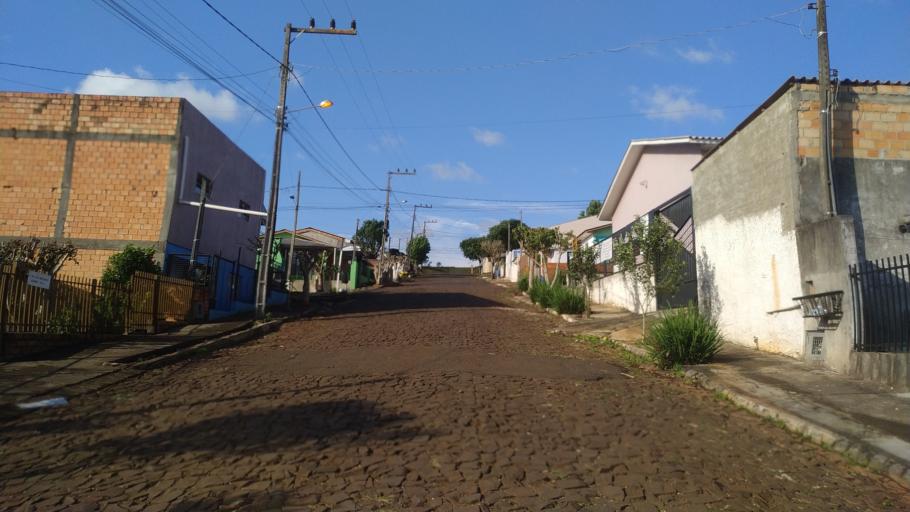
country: BR
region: Santa Catarina
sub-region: Chapeco
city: Chapeco
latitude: -27.0681
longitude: -52.6082
